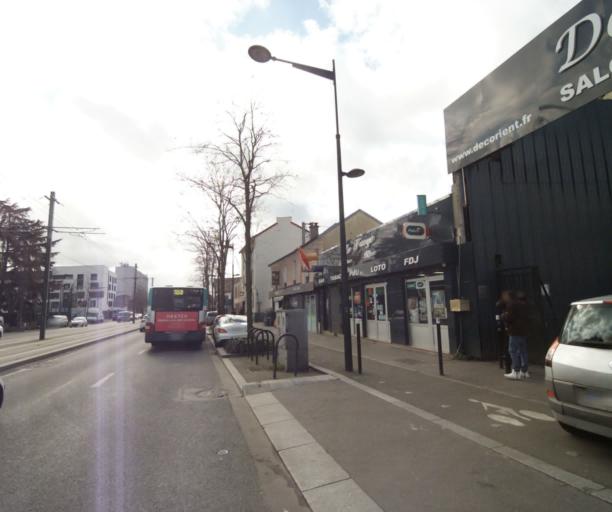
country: FR
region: Ile-de-France
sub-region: Departement de Seine-Saint-Denis
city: Pierrefitte-sur-Seine
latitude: 48.9580
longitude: 2.3585
